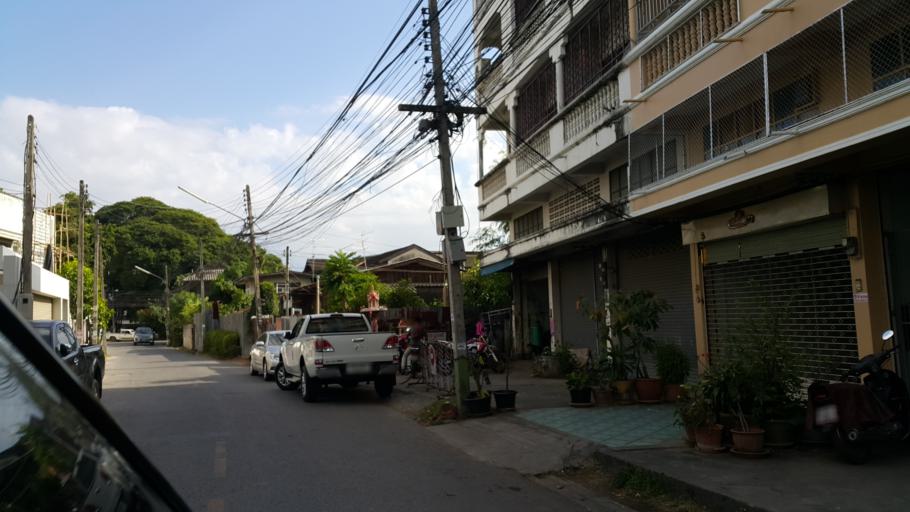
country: TH
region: Chiang Mai
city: Chiang Mai
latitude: 18.7864
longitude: 99.0071
